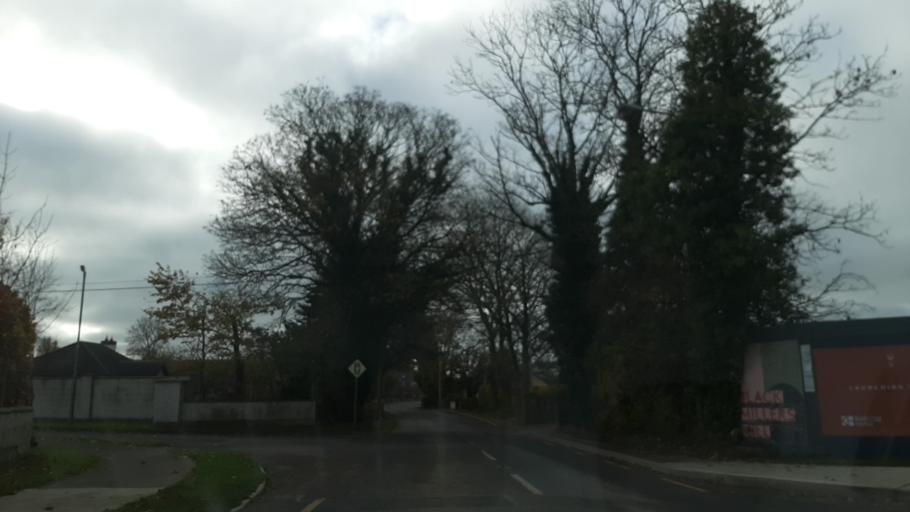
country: IE
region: Leinster
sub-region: Kildare
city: Kildare
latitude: 53.1699
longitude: -6.9019
